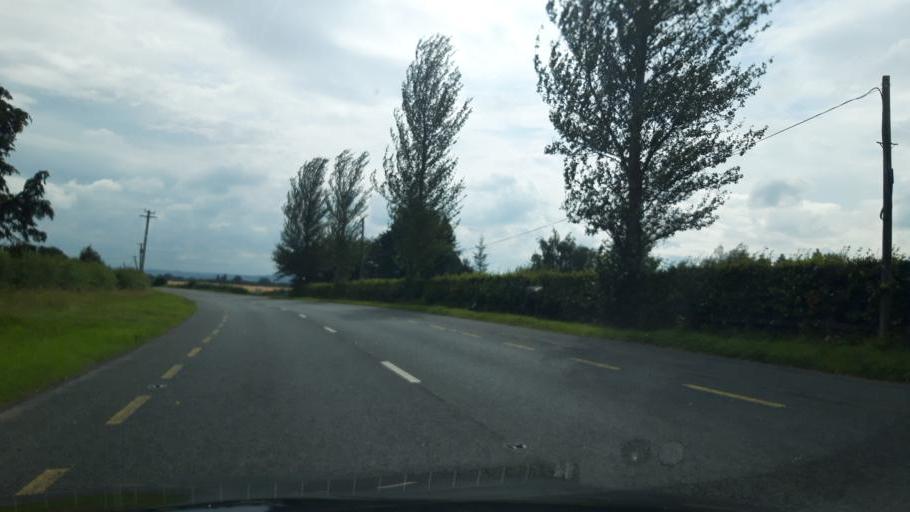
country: IE
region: Leinster
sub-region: Kildare
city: Athy
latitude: 52.9767
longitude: -7.0129
